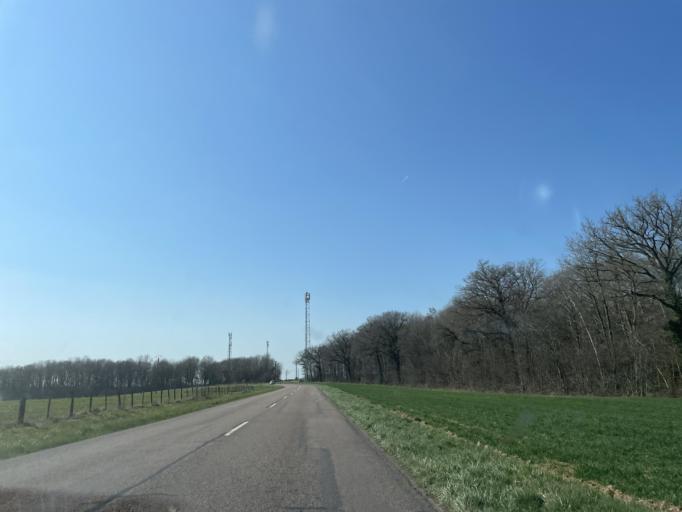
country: FR
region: Bourgogne
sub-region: Departement de la Cote-d'Or
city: Semur-en-Auxois
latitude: 47.4450
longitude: 4.3160
